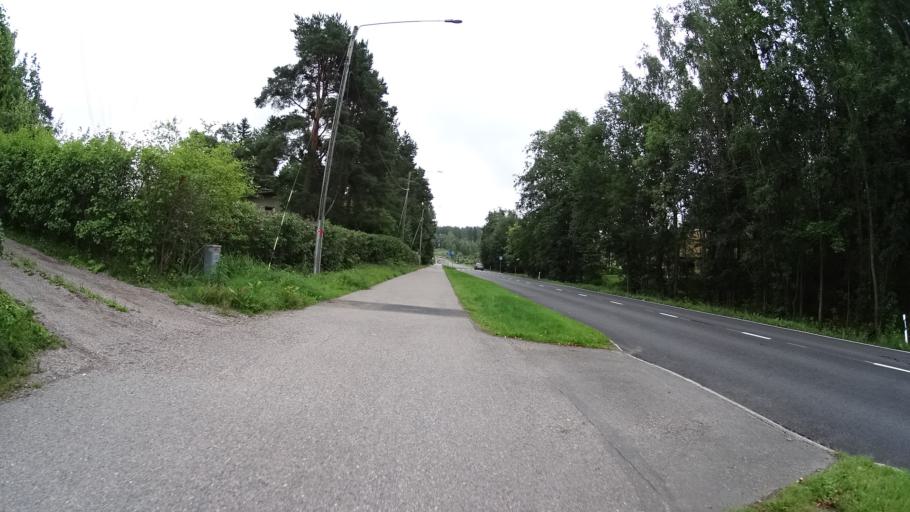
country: FI
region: Uusimaa
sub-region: Helsinki
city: Kilo
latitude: 60.2396
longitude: 24.7673
